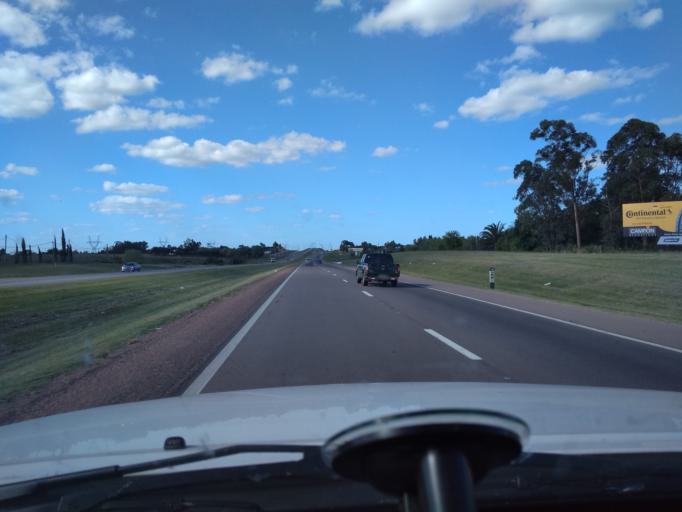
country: UY
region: Canelones
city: Las Piedras
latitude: -34.7369
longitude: -56.2507
